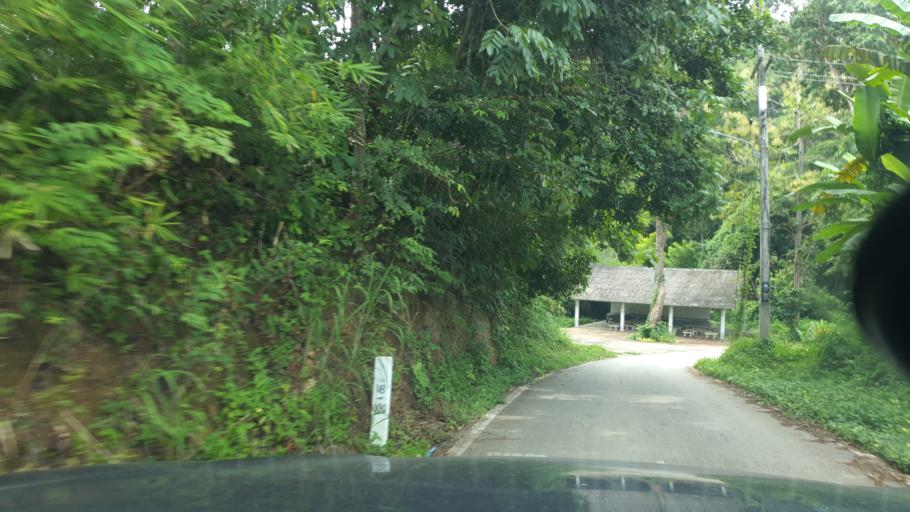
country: TH
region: Lampang
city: Hang Chat
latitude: 18.4256
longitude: 99.2649
